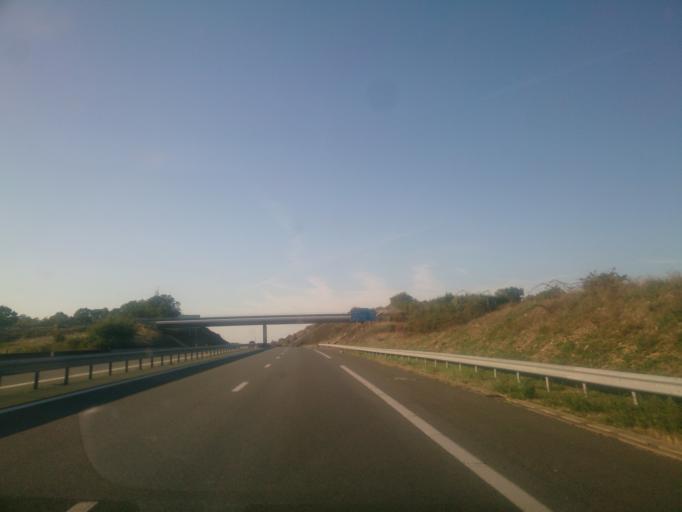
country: FR
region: Midi-Pyrenees
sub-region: Departement du Lot
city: Le Vigan
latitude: 44.7080
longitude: 1.5719
